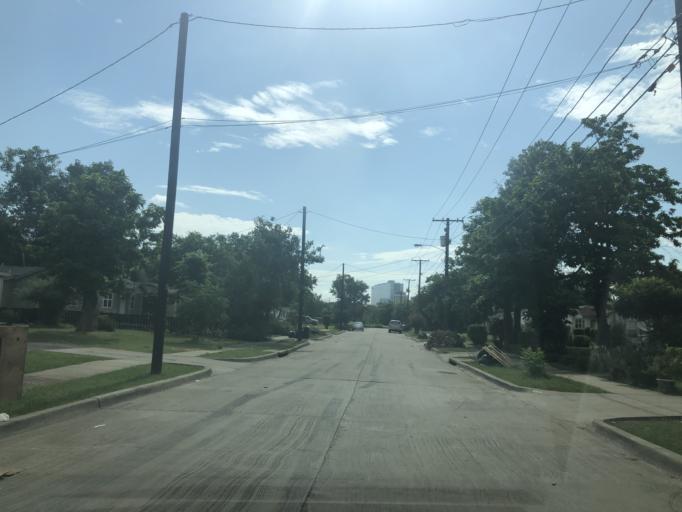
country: US
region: Texas
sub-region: Dallas County
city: Dallas
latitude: 32.8136
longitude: -96.8516
